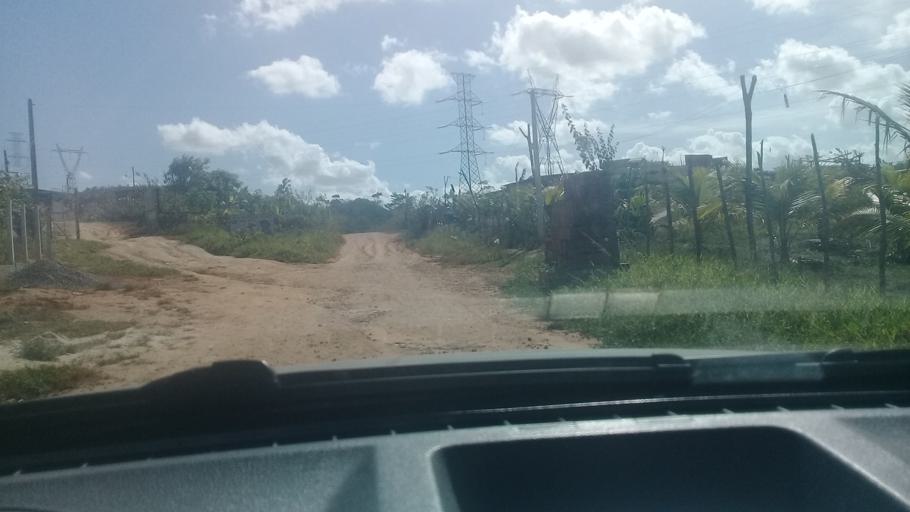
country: BR
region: Pernambuco
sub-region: Jaboatao Dos Guararapes
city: Jaboatao dos Guararapes
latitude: -8.0861
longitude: -35.0328
